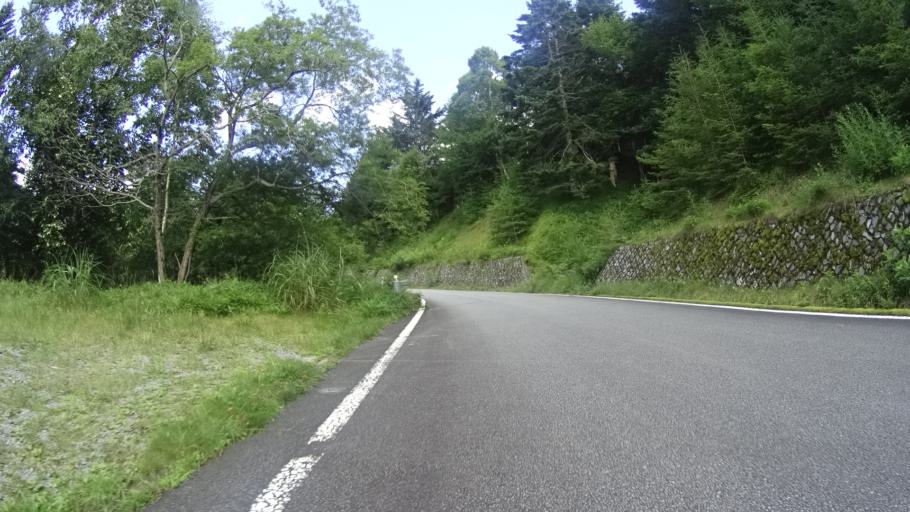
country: JP
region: Yamanashi
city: Enzan
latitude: 35.8434
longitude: 138.6420
